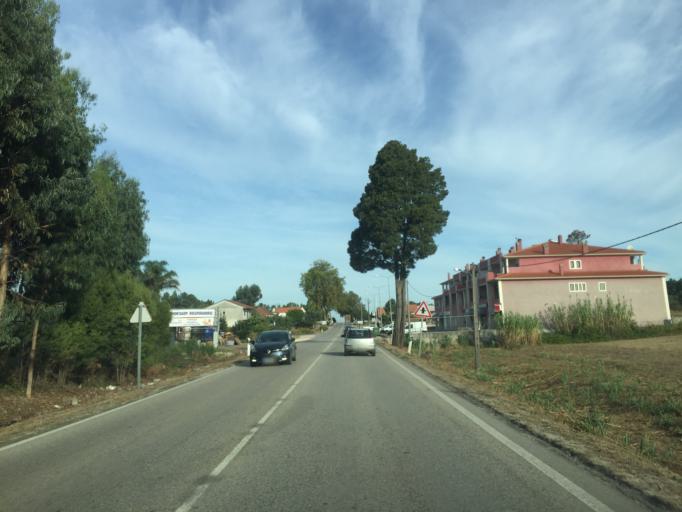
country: PT
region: Leiria
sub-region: Pombal
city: Lourical
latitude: 39.9599
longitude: -8.7877
